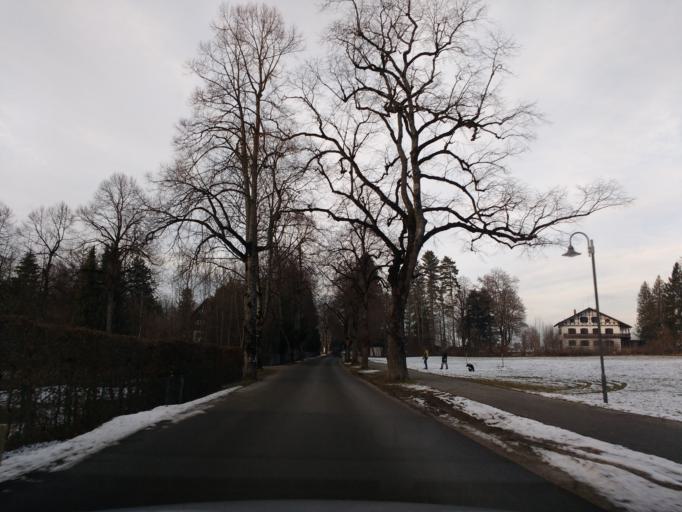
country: DE
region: Bavaria
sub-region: Swabia
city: Schwangau
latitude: 47.5594
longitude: 10.7394
